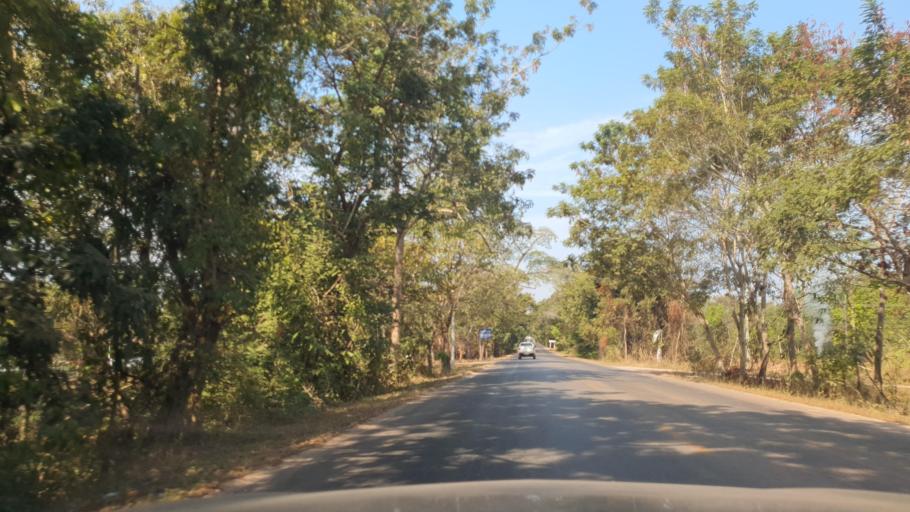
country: TH
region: Nakhon Phanom
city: Ban Phaeng
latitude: 18.0195
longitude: 104.1515
